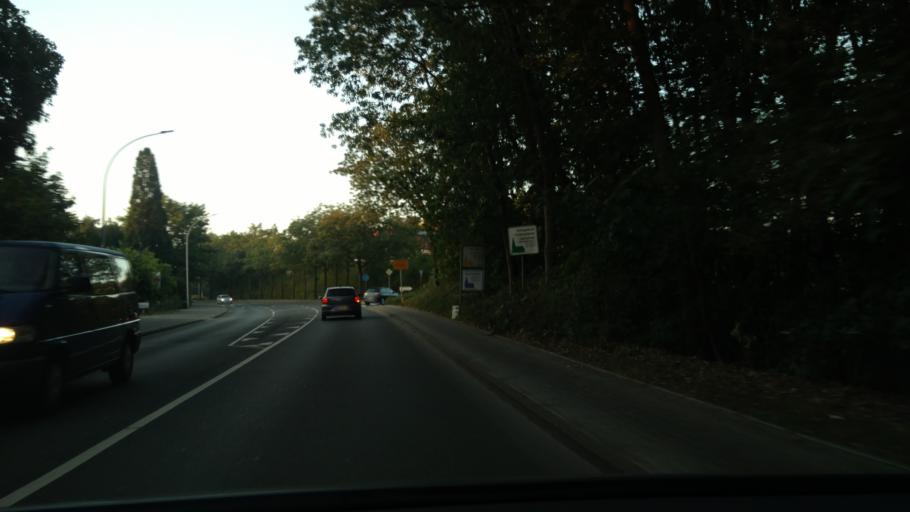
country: DE
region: North Rhine-Westphalia
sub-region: Regierungsbezirk Munster
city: Borken
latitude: 51.8536
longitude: 6.8427
